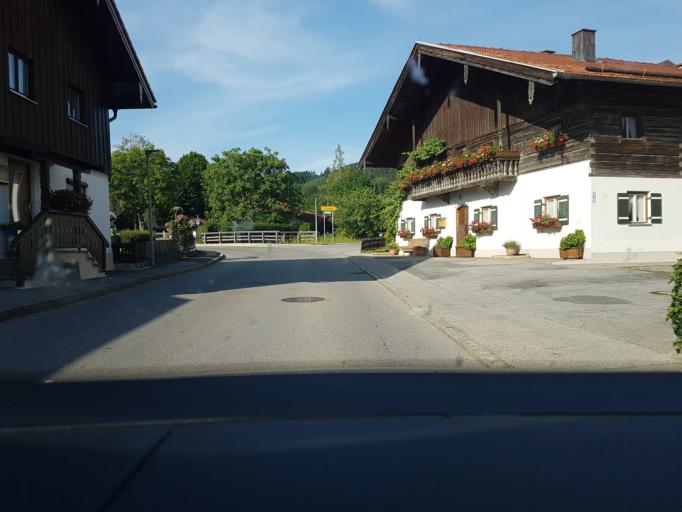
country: DE
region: Bavaria
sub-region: Upper Bavaria
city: Teisendorf
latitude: 47.8518
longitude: 12.7854
